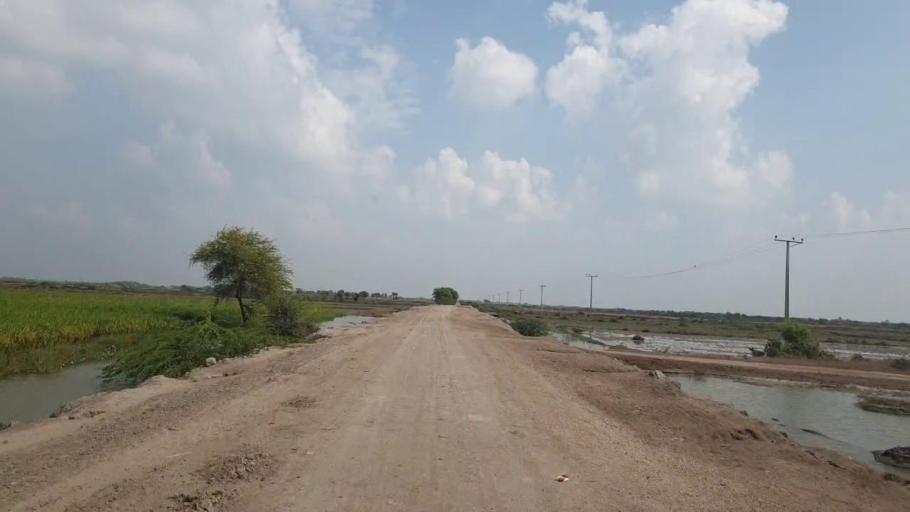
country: PK
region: Sindh
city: Badin
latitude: 24.5327
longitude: 68.6194
